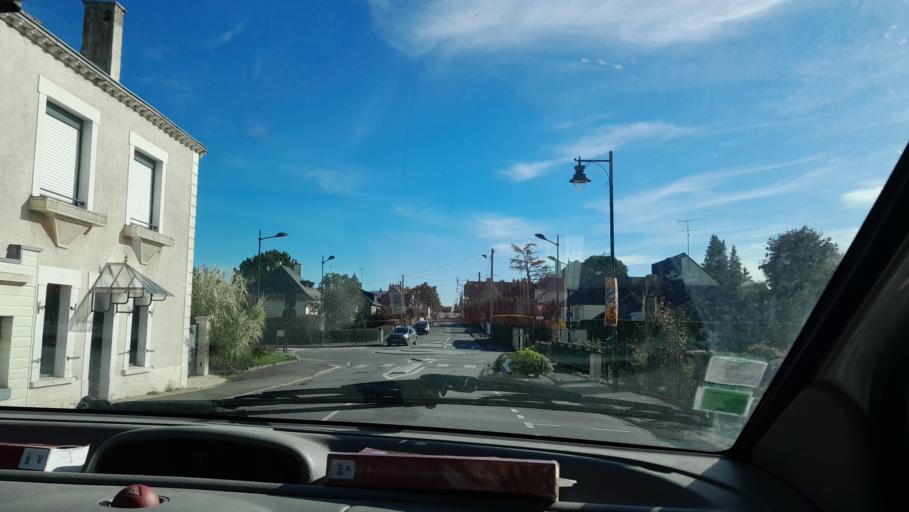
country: FR
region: Brittany
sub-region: Departement d'Ille-et-Vilaine
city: Argentre-du-Plessis
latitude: 48.0541
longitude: -1.1503
